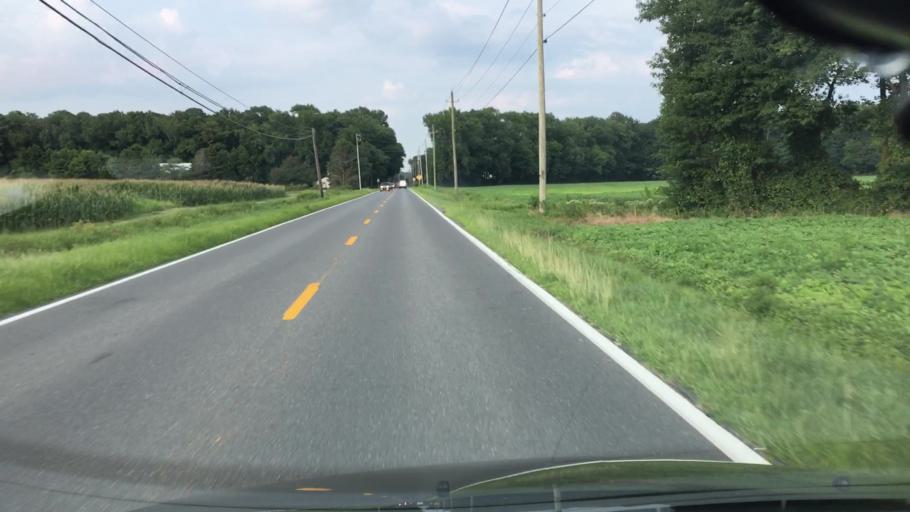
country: US
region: Delaware
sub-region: Sussex County
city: Selbyville
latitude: 38.4348
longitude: -75.2071
